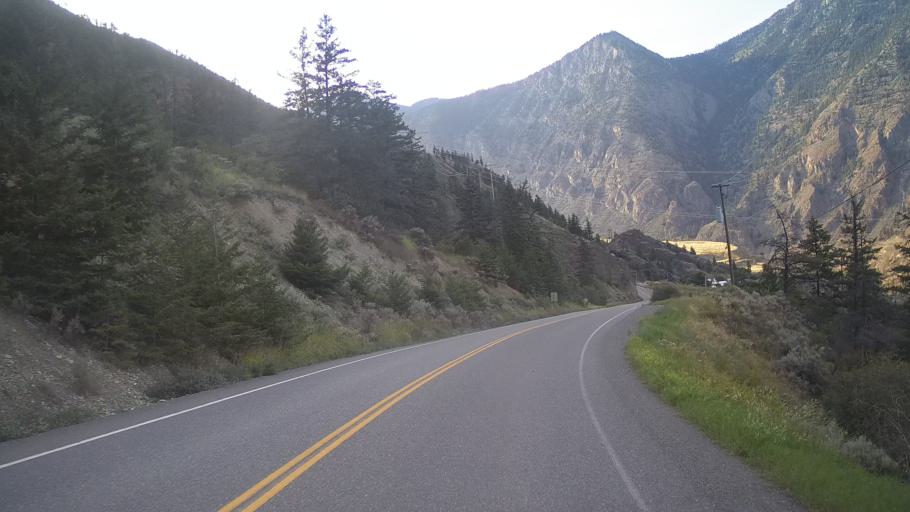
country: CA
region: British Columbia
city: Lillooet
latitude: 50.7453
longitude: -121.8907
